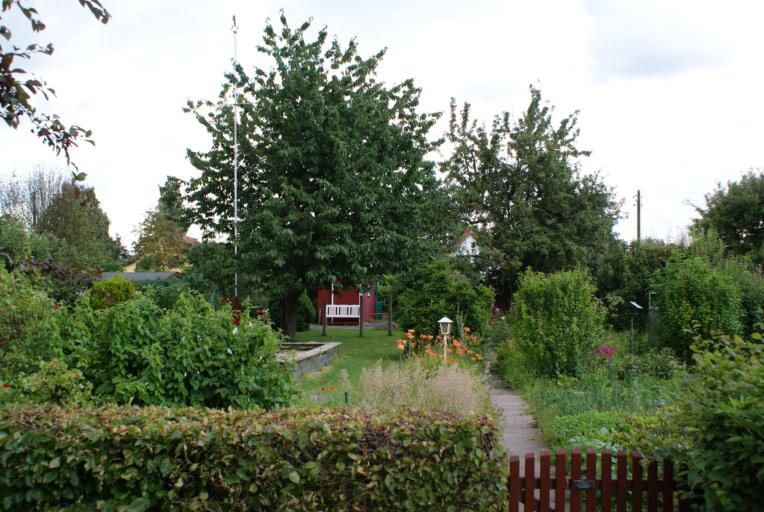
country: DE
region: Lower Saxony
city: Stuhr
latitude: 53.0922
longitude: 8.7444
